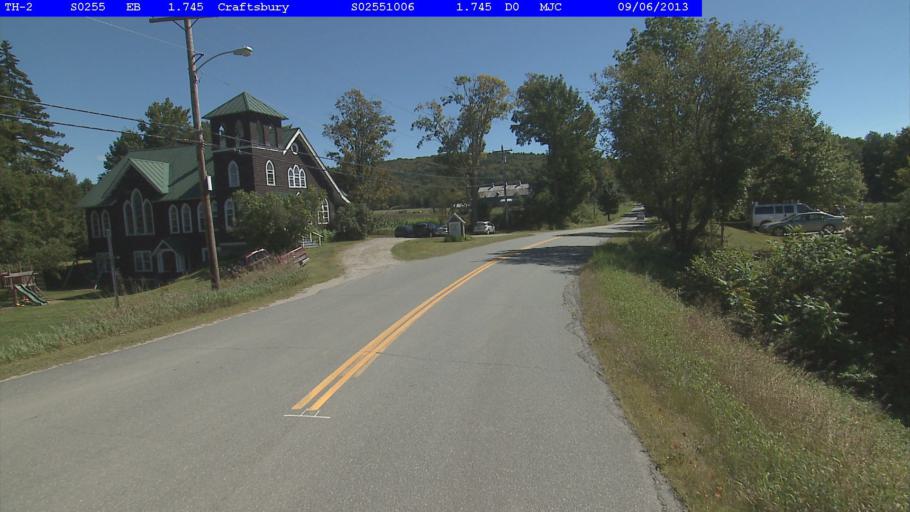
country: US
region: Vermont
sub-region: Caledonia County
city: Hardwick
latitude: 44.6413
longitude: -72.3422
